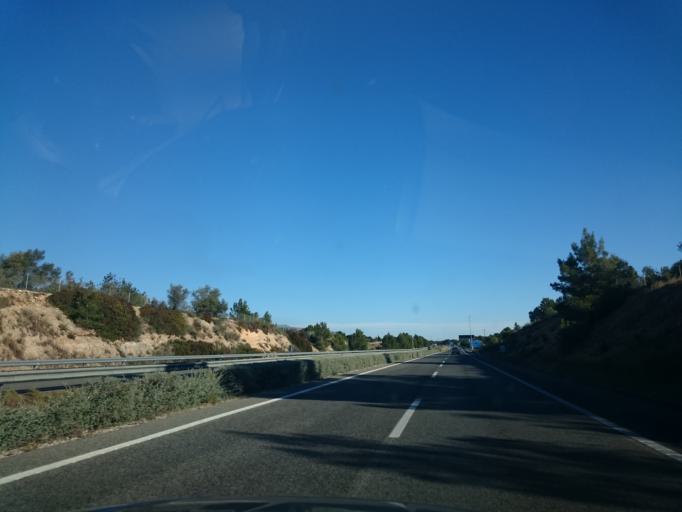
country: ES
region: Catalonia
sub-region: Provincia de Tarragona
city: l'Ametlla de Mar
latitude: 40.8723
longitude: 0.7841
